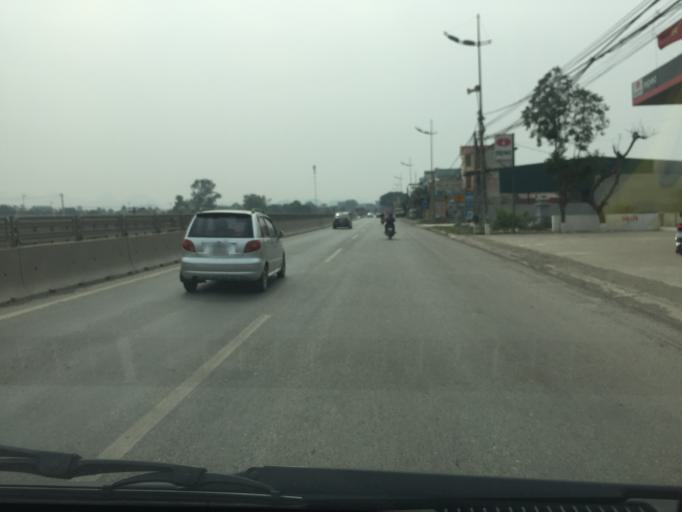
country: VN
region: Ninh Binh
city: Thi Tran Tam Diep
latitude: 20.1748
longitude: 105.9472
